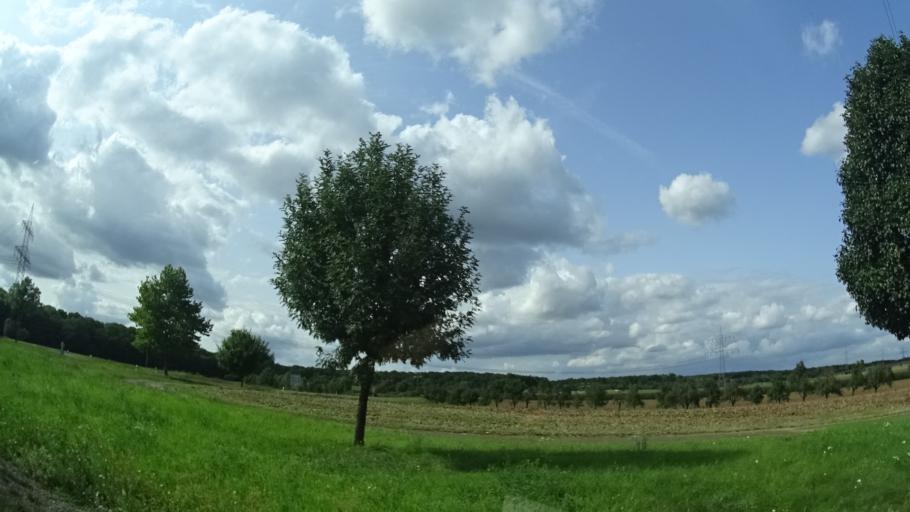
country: DE
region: Bavaria
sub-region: Regierungsbezirk Unterfranken
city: Bergrheinfeld
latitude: 49.9989
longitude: 10.1655
